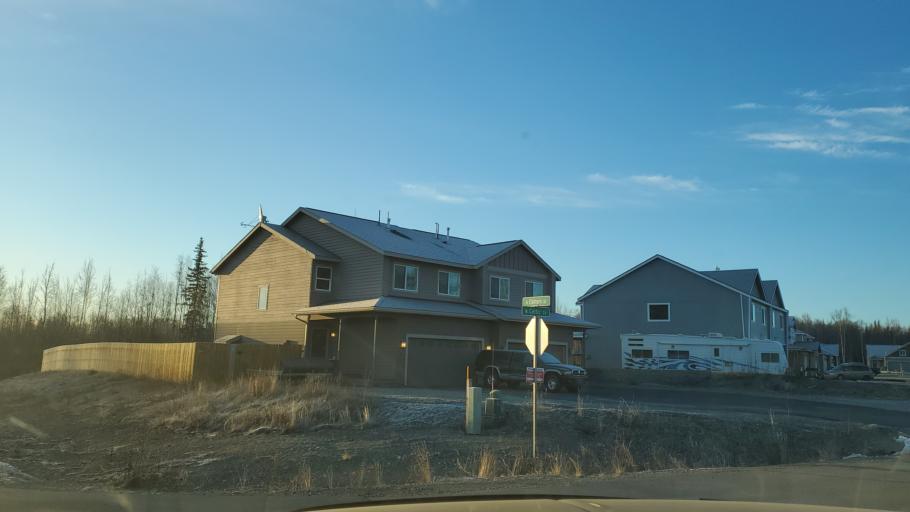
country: US
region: Alaska
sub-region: Matanuska-Susitna Borough
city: Wasilla
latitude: 61.5901
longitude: -149.4535
